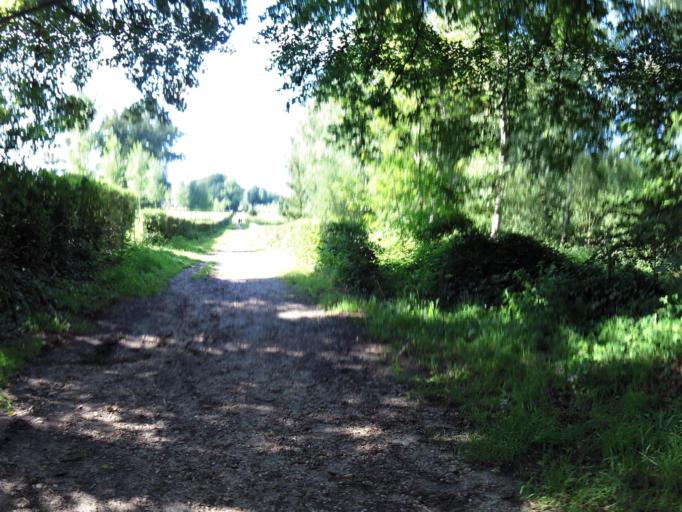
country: BE
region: Flanders
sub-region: Provincie Limburg
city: Tongeren
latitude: 50.7812
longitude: 5.4530
